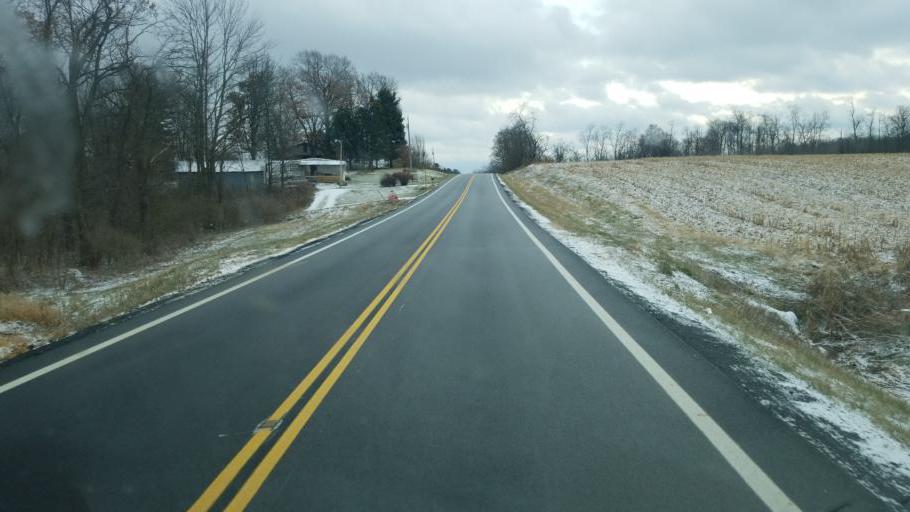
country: US
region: Ohio
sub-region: Licking County
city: Utica
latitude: 40.2825
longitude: -82.3713
